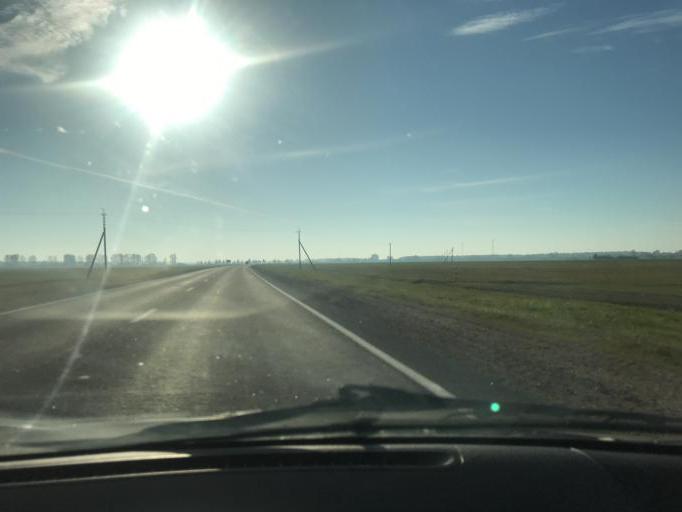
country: BY
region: Brest
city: Drahichyn
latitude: 52.1760
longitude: 25.3104
